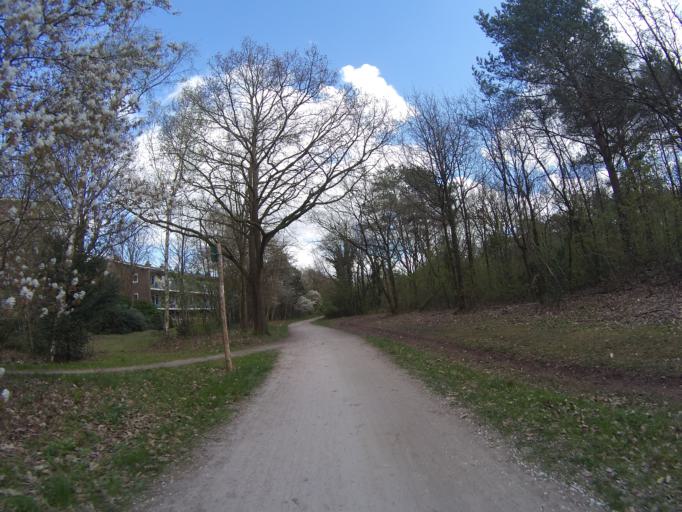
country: NL
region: North Holland
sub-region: Gemeente Bussum
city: Bussum
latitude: 52.2655
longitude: 5.1904
